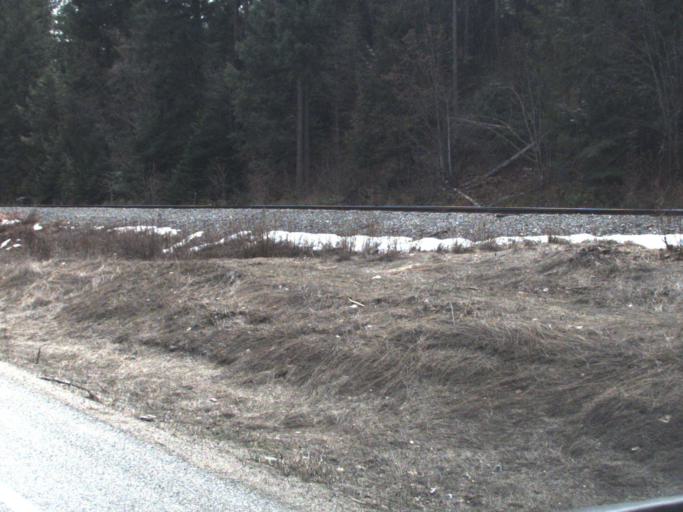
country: US
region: Washington
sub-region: Pend Oreille County
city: Newport
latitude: 48.2336
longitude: -117.2183
